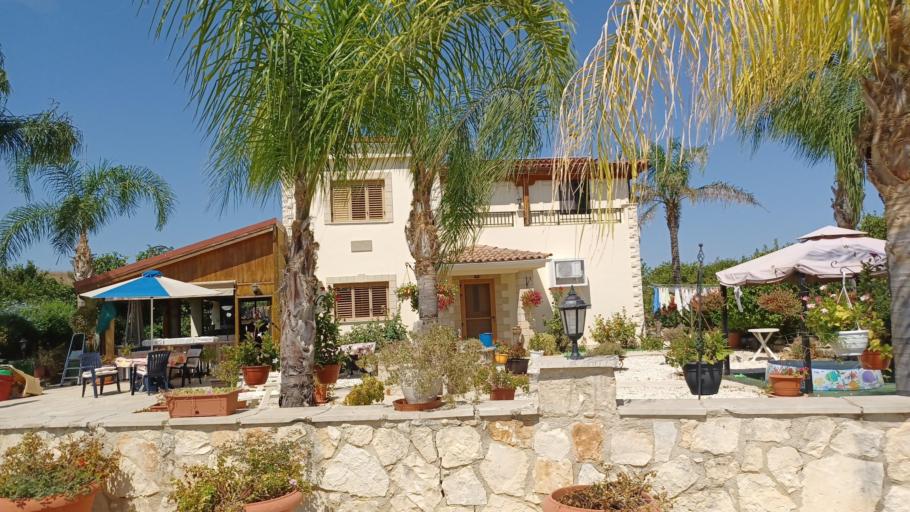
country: CY
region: Pafos
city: Polis
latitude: 35.0128
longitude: 32.4310
